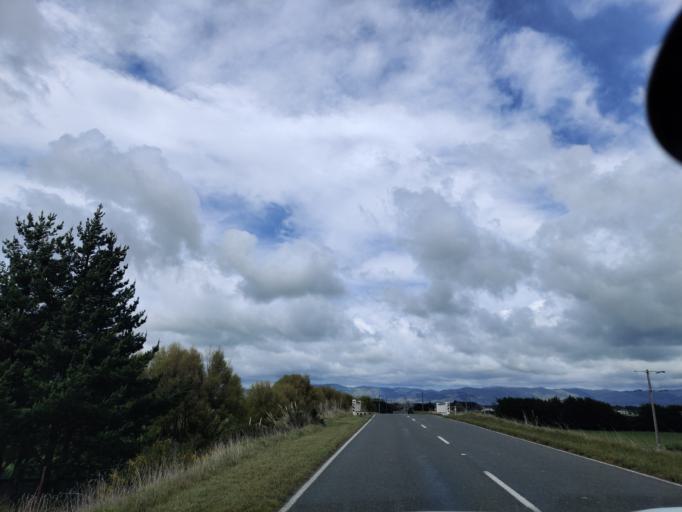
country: NZ
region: Manawatu-Wanganui
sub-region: Palmerston North City
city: Palmerston North
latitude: -40.3667
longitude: 175.5528
